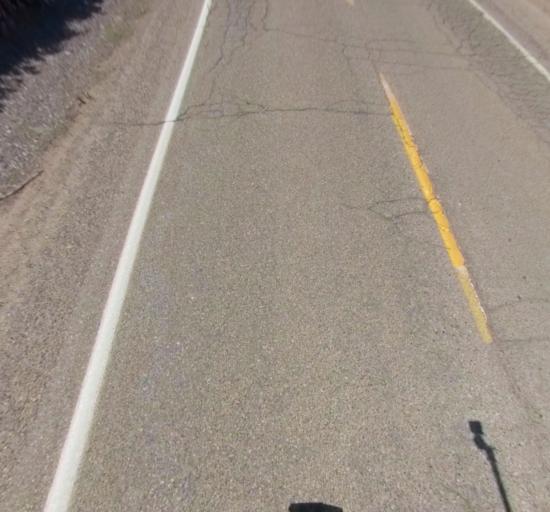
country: US
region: California
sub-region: Madera County
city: Madera
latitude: 36.9302
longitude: -120.2015
